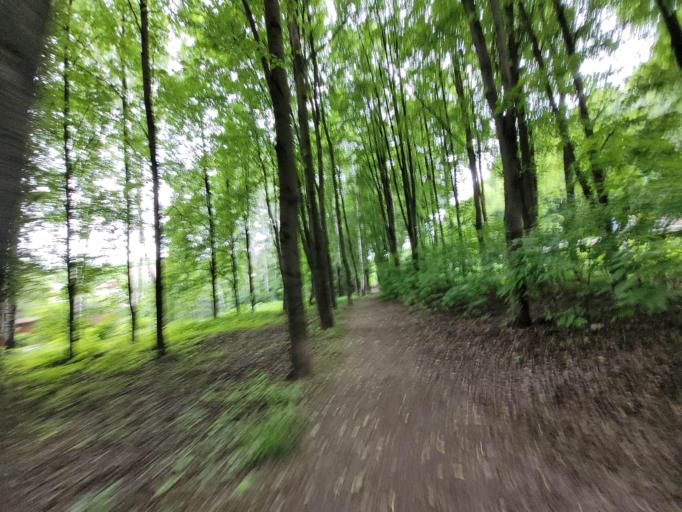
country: RU
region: Moskovskaya
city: Lesnyye Polyany
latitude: 55.9471
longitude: 37.8606
